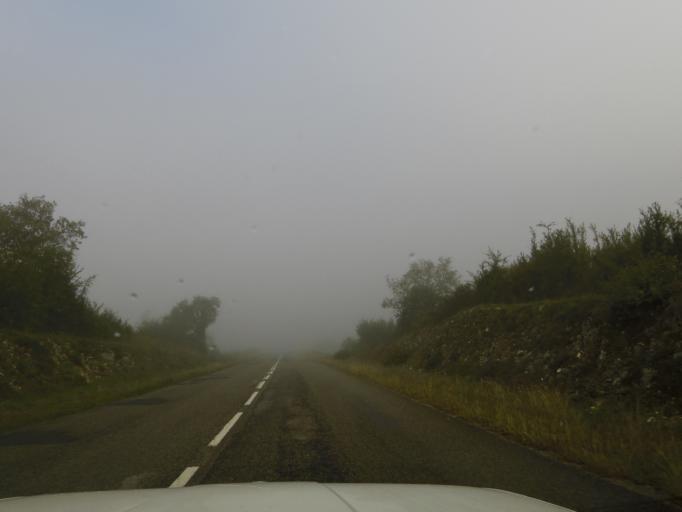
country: FR
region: Rhone-Alpes
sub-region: Departement de l'Isere
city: Creys-Mepieu
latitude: 45.7491
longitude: 5.5049
